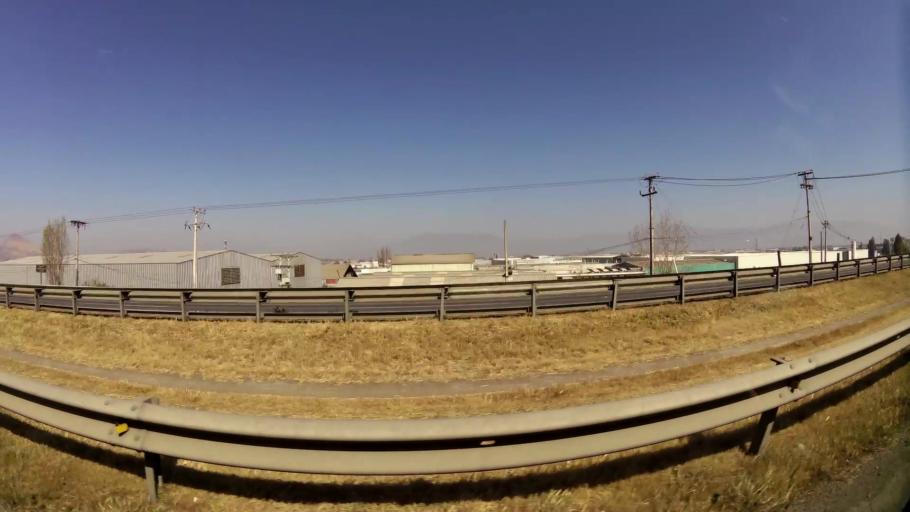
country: CL
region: Santiago Metropolitan
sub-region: Provincia de Chacabuco
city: Chicureo Abajo
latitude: -33.3333
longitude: -70.6940
